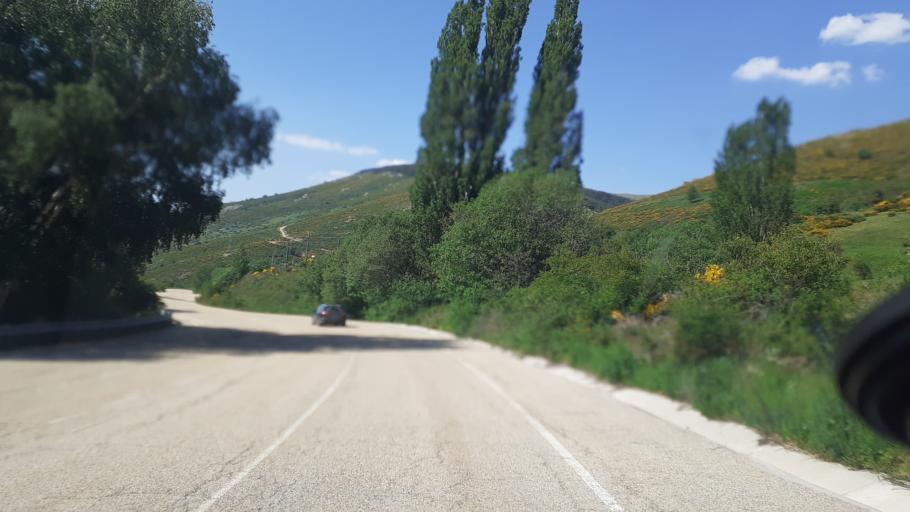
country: ES
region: Madrid
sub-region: Provincia de Madrid
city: Somosierra
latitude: 41.1389
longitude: -3.5787
